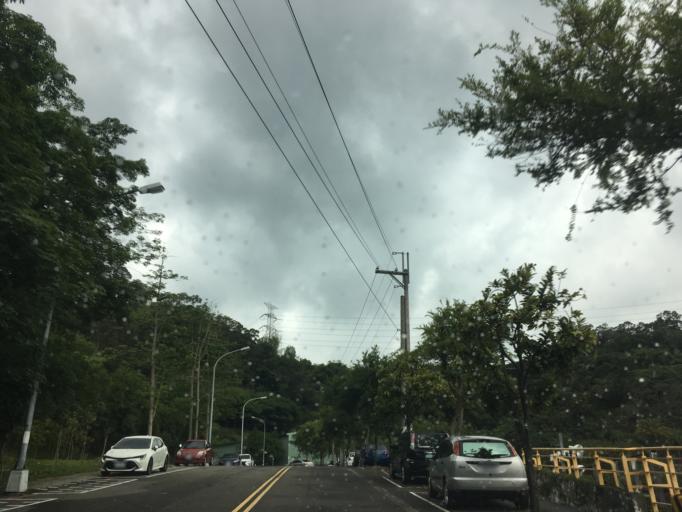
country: TW
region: Taiwan
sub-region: Taichung City
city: Taichung
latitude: 24.0677
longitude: 120.7165
